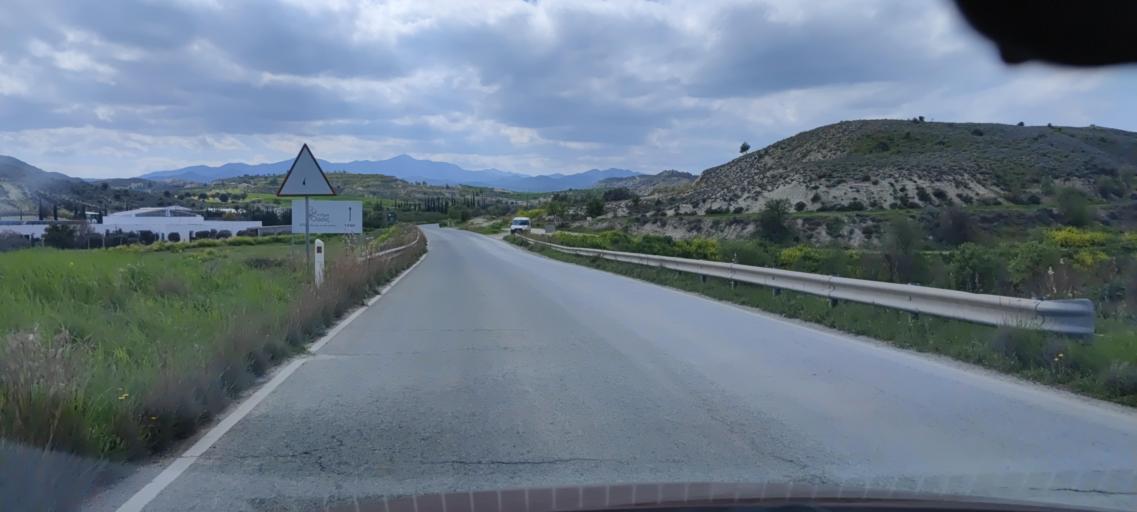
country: CY
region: Lefkosia
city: Tseri
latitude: 35.0290
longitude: 33.3068
